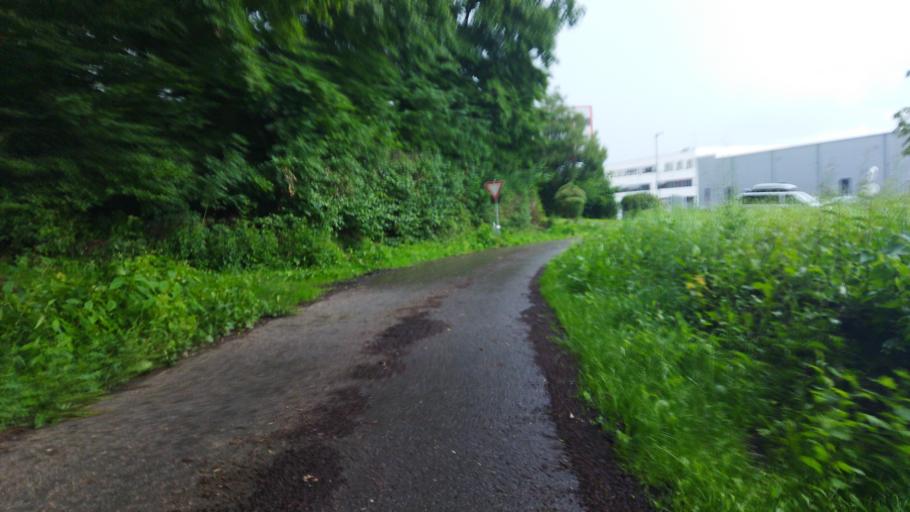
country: DE
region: Baden-Wuerttemberg
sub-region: Regierungsbezirk Stuttgart
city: Kirchardt
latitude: 49.2010
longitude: 9.0046
